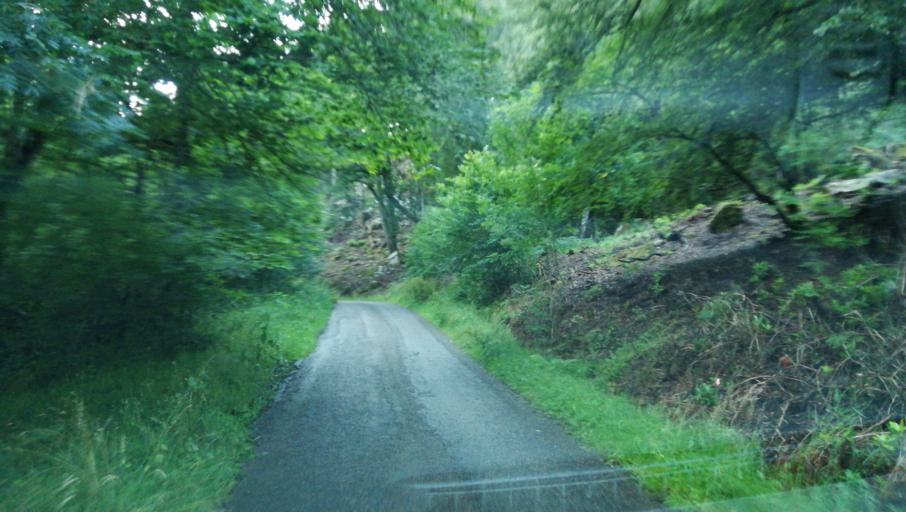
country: GB
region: Scotland
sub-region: Highland
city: Spean Bridge
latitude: 57.0692
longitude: -4.8172
